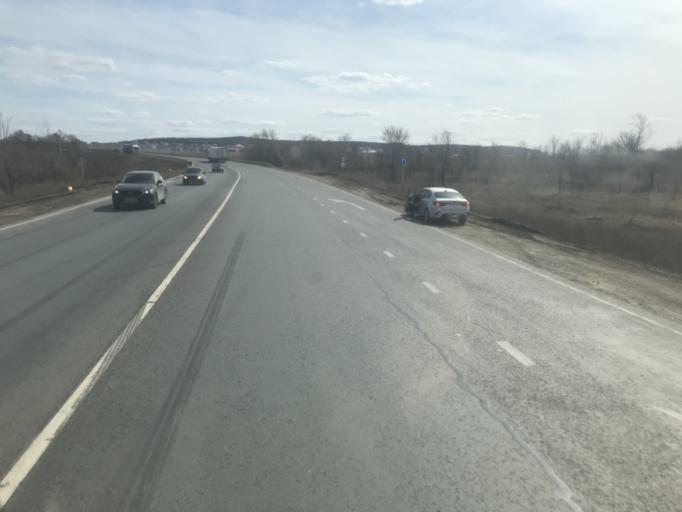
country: RU
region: Samara
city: Novosemeykino
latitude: 53.4109
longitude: 50.3504
